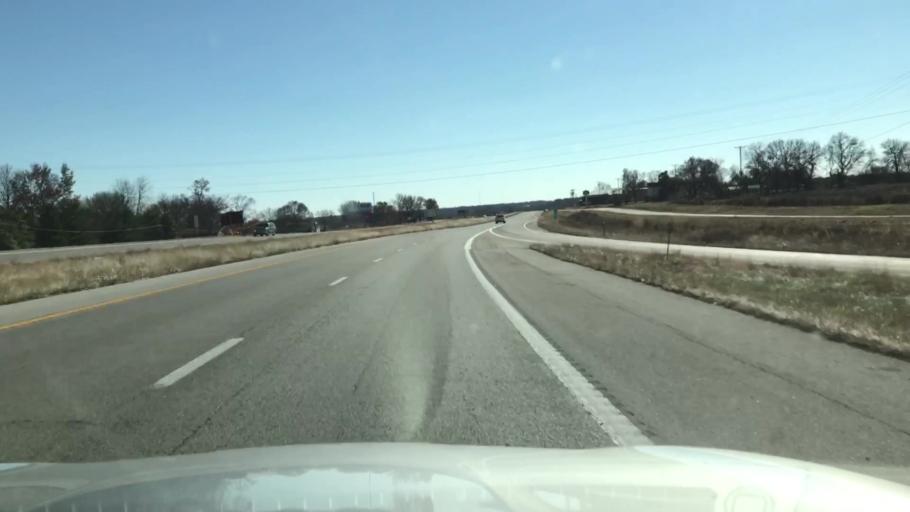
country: US
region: Missouri
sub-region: Jasper County
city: Carthage
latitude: 37.1283
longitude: -94.3110
